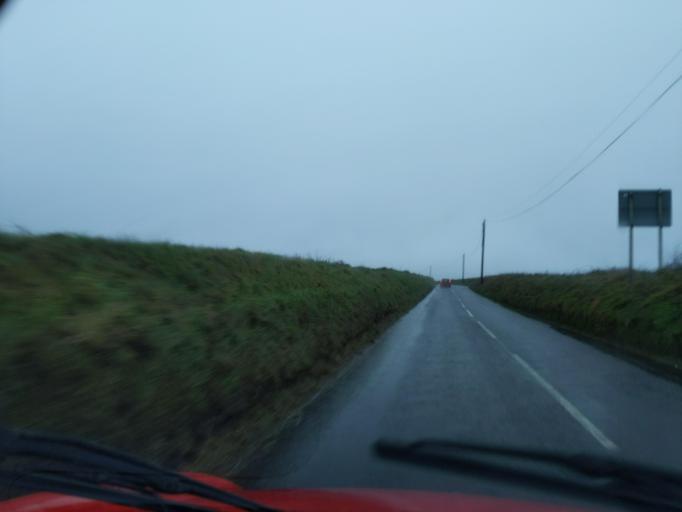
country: GB
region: England
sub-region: Cornwall
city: Camelford
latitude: 50.6409
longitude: -4.6946
